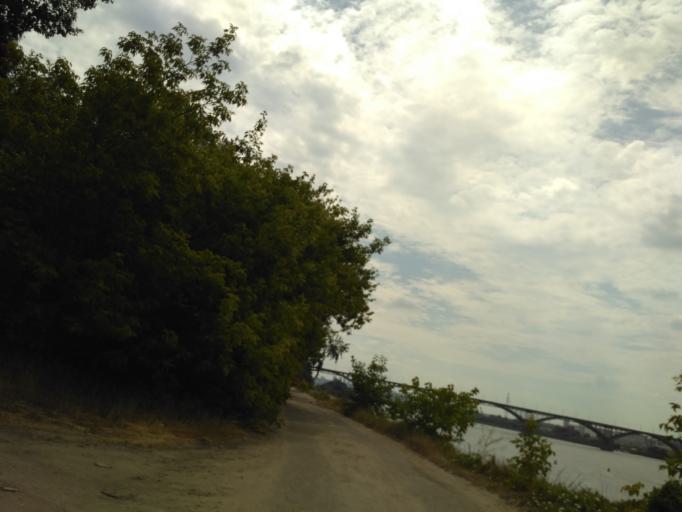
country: RU
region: Nizjnij Novgorod
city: Nizhniy Novgorod
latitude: 56.3075
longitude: 43.9681
